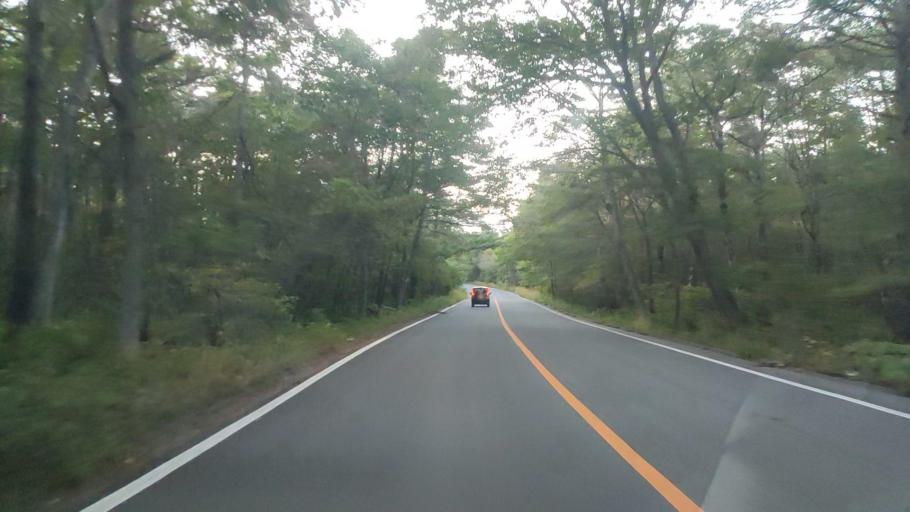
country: JP
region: Nagano
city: Komoro
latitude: 36.4114
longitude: 138.5703
